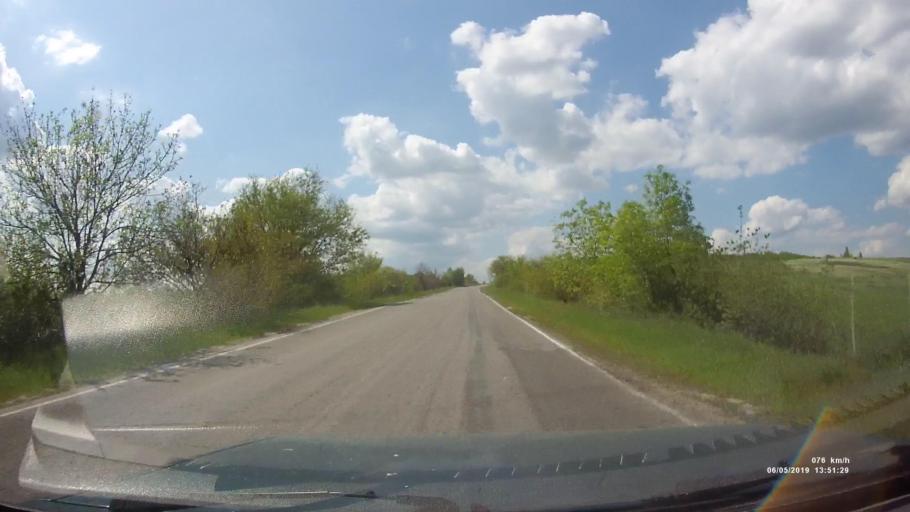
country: RU
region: Rostov
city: Melikhovskaya
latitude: 47.6572
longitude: 40.4913
